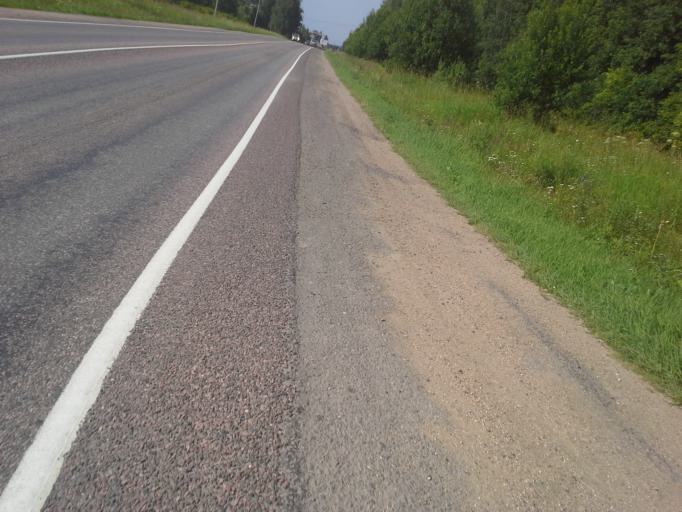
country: RU
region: Moskovskaya
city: Istra
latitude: 55.8721
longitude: 36.7978
